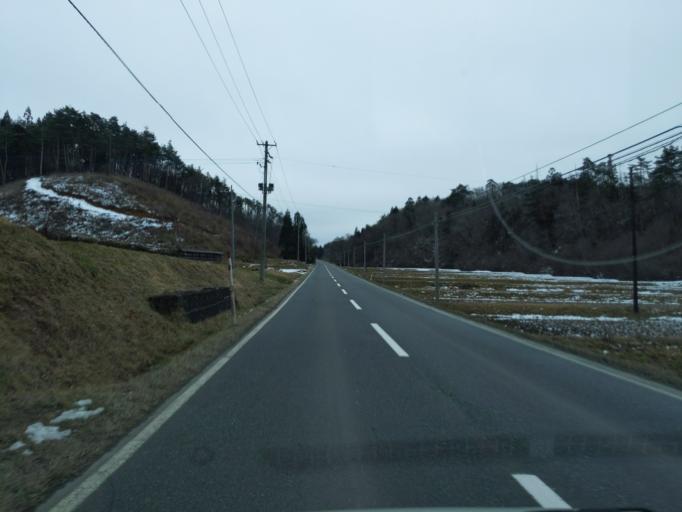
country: JP
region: Iwate
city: Mizusawa
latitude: 39.1490
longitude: 141.2430
